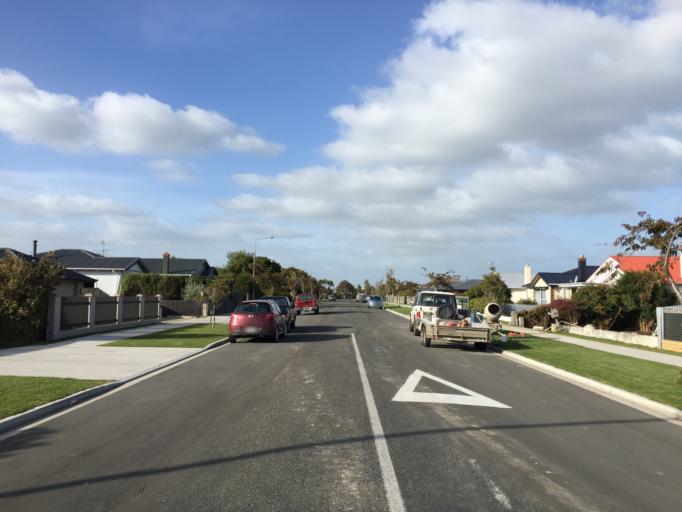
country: NZ
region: Southland
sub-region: Invercargill City
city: Invercargill
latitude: -46.4084
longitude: 168.3697
